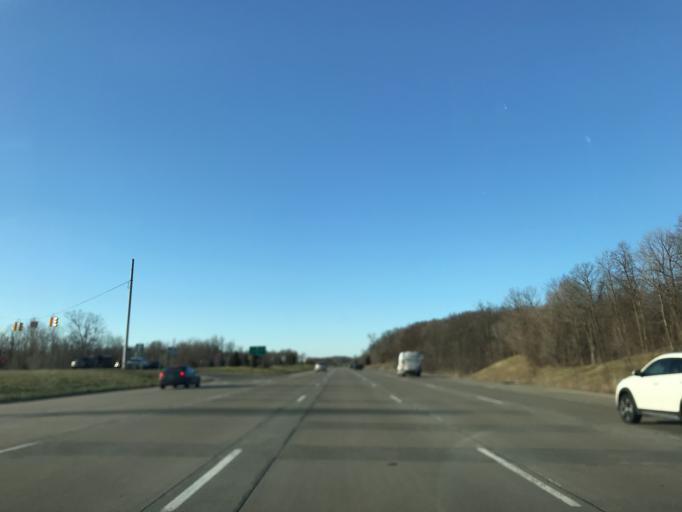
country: US
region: Michigan
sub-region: Oakland County
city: Walled Lake
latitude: 42.5261
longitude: -83.4456
